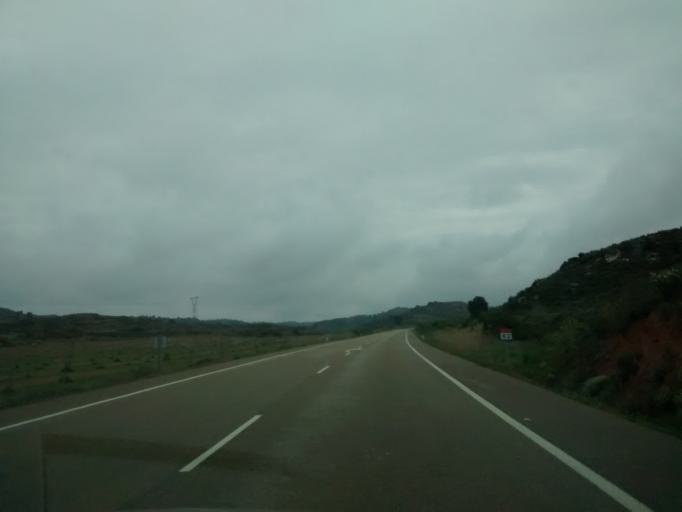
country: ES
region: Aragon
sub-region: Provincia de Zaragoza
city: Caspe
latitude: 41.2085
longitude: 0.0267
